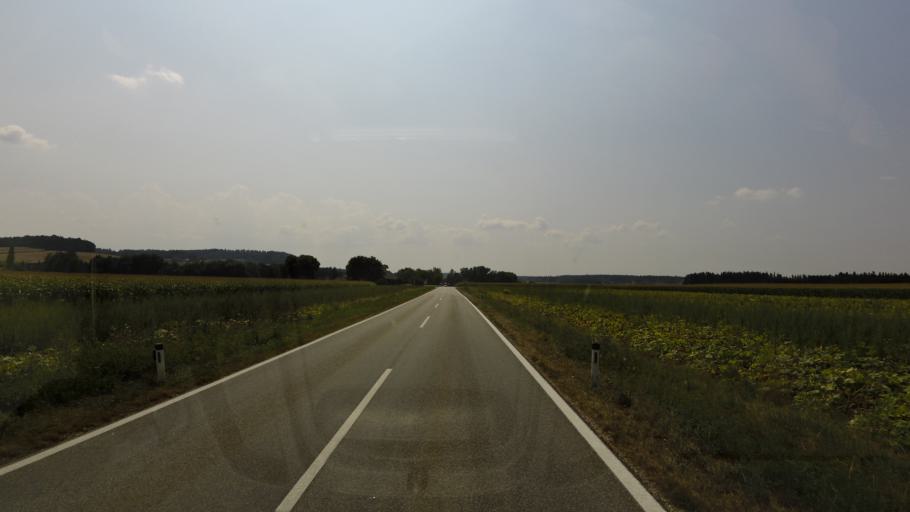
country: DE
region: Bavaria
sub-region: Lower Bavaria
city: Bad Fussing
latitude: 48.2694
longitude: 13.3295
